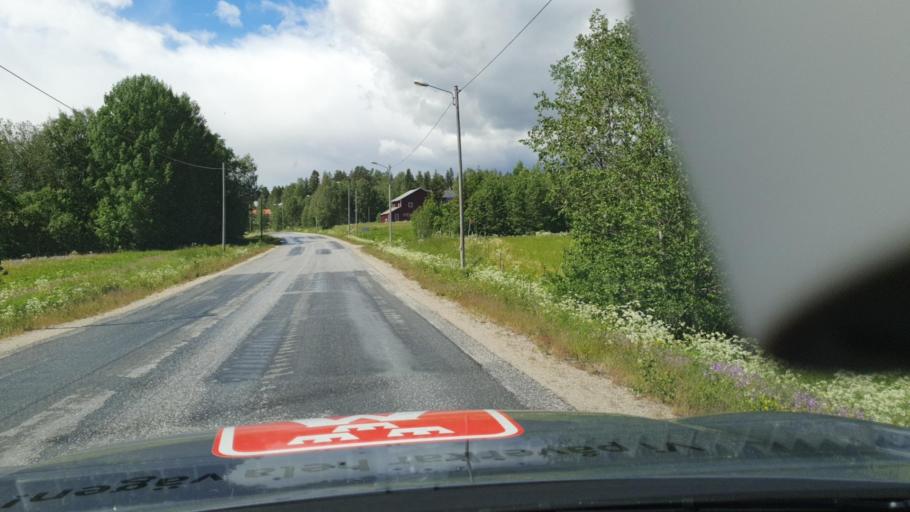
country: SE
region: Vaesternorrland
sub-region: OErnskoeldsviks Kommun
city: Bredbyn
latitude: 63.3750
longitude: 17.9247
